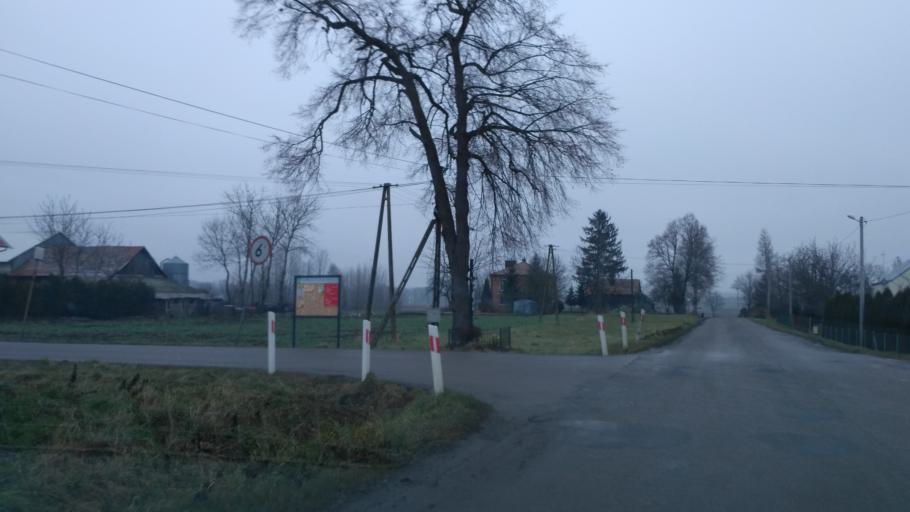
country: PL
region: Subcarpathian Voivodeship
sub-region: Powiat przeworski
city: Zarzecze
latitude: 49.9745
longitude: 22.5530
